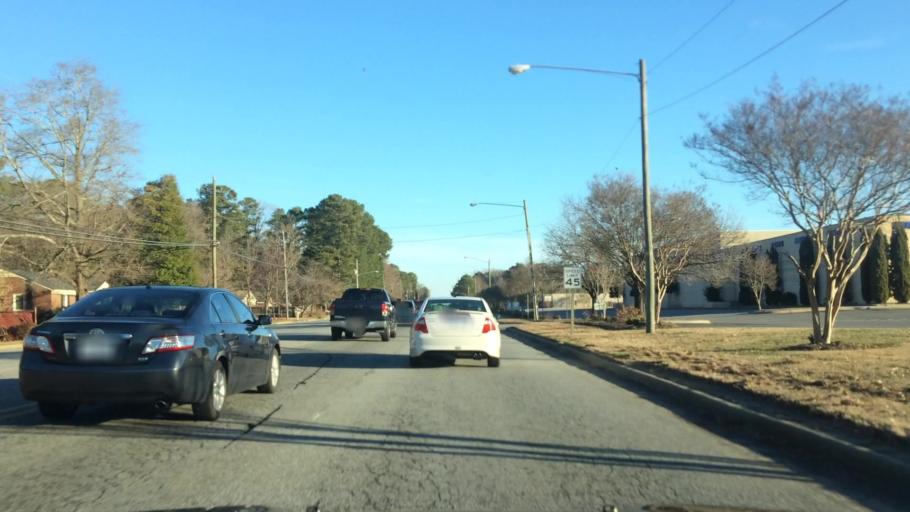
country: US
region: North Carolina
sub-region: Pitt County
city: Summerfield
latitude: 35.5815
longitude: -77.3806
